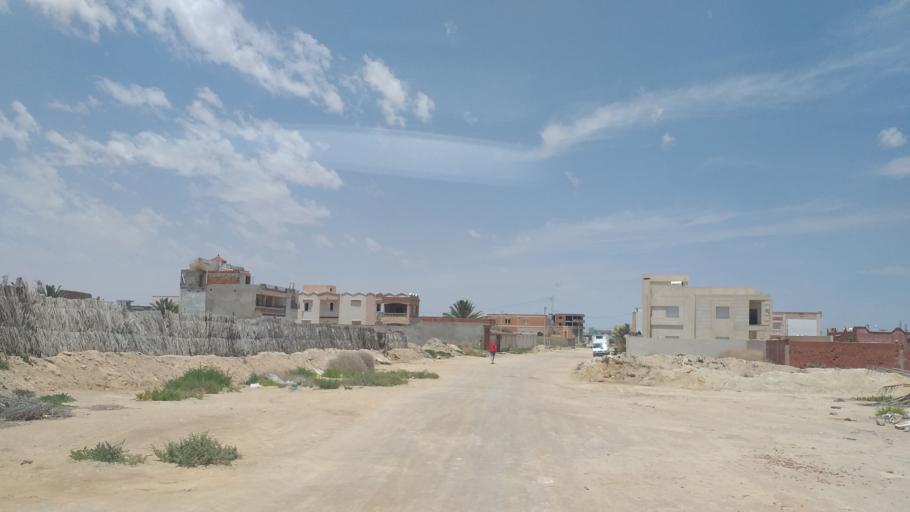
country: TN
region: Qabis
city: Gabes
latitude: 33.9499
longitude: 10.0725
